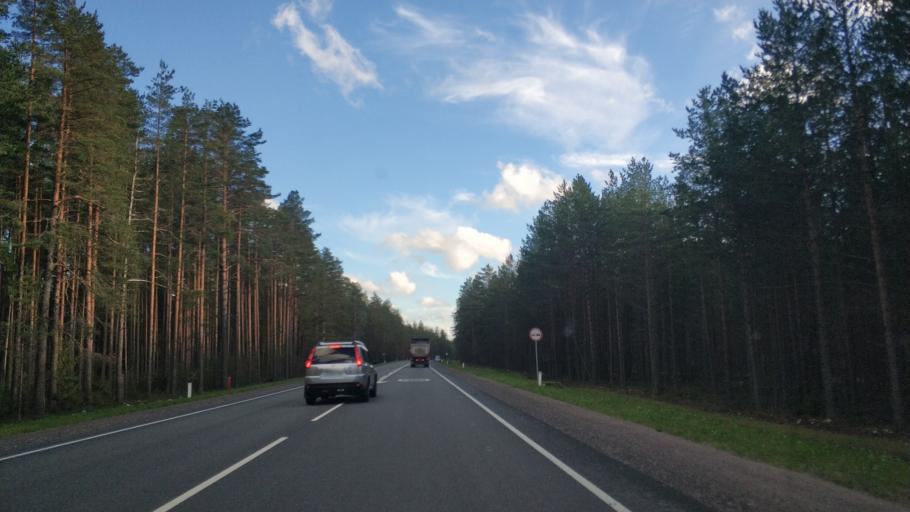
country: RU
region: Leningrad
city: Priozersk
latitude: 60.8882
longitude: 30.1602
